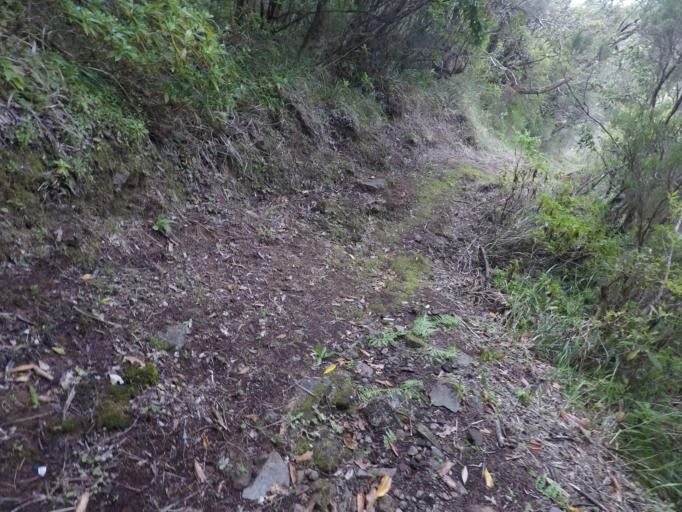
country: PT
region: Madeira
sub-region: Camara de Lobos
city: Curral das Freiras
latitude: 32.7688
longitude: -16.9759
